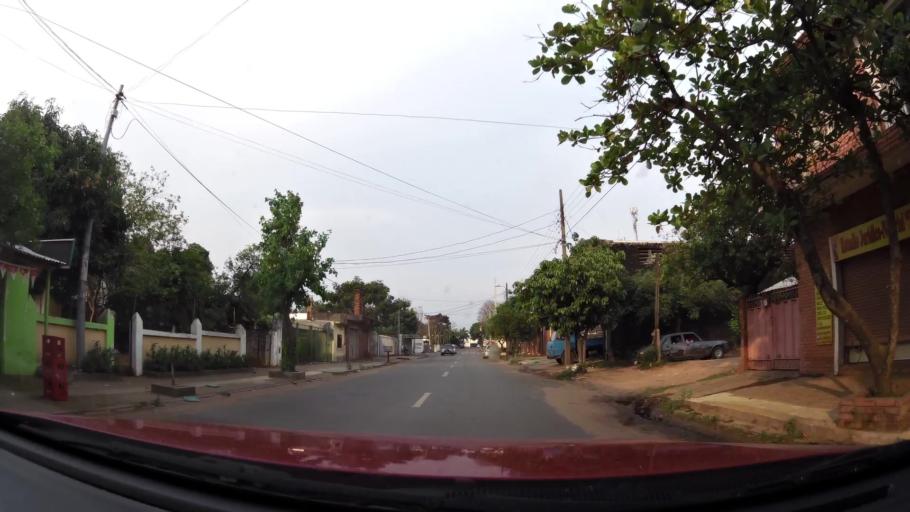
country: PY
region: Central
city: Lambare
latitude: -25.3309
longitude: -57.5754
